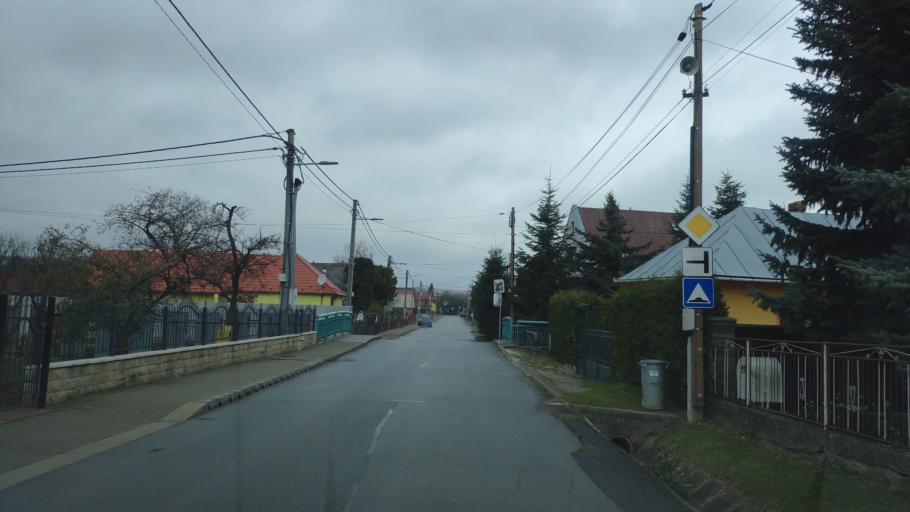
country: SK
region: Presovsky
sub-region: Okres Presov
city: Presov
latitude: 49.0079
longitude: 21.1846
